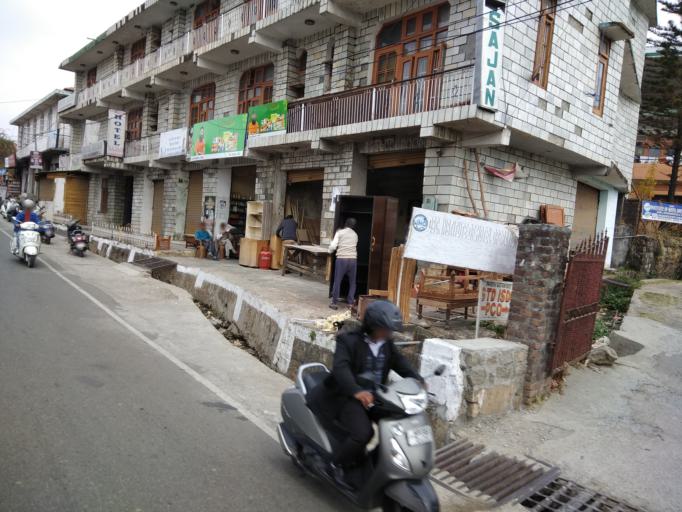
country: IN
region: Himachal Pradesh
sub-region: Kangra
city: Dharmsala
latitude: 32.2017
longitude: 76.3338
